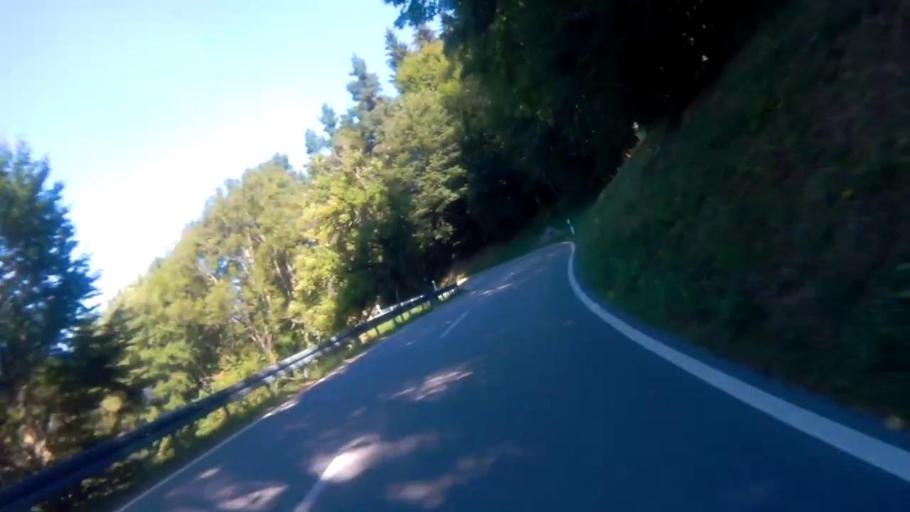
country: DE
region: Baden-Wuerttemberg
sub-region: Freiburg Region
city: Badenweiler
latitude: 47.7774
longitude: 7.7384
